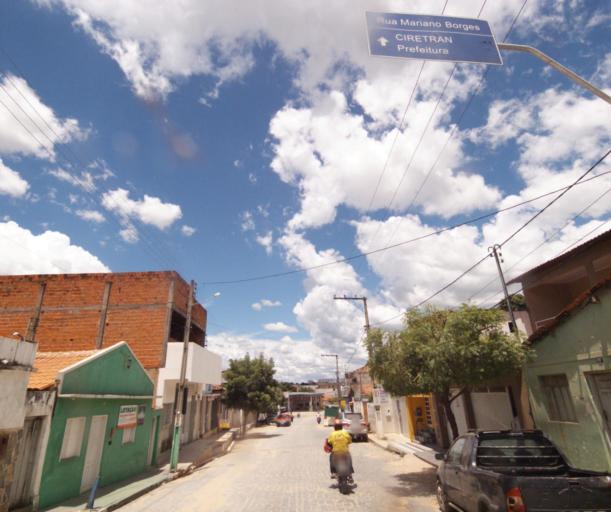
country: BR
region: Bahia
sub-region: Sao Felix Do Coribe
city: Santa Maria da Vitoria
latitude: -13.3982
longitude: -44.2028
